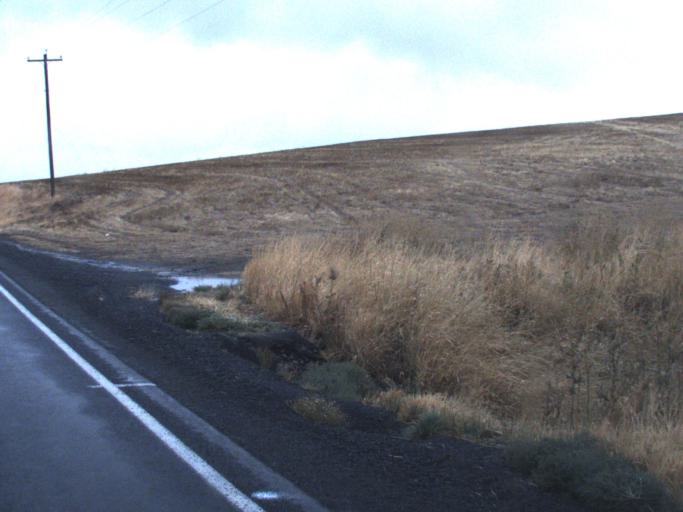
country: US
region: Washington
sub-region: Whitman County
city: Colfax
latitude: 47.0885
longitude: -117.5628
